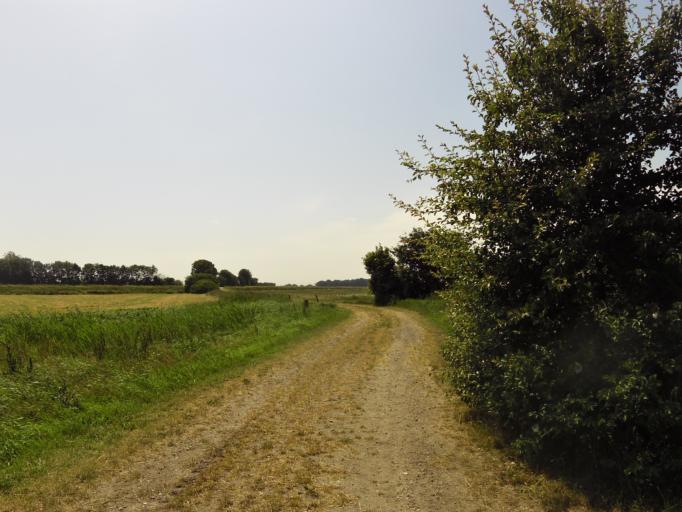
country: DK
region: South Denmark
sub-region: Haderslev Kommune
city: Vojens
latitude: 55.1552
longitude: 9.2493
